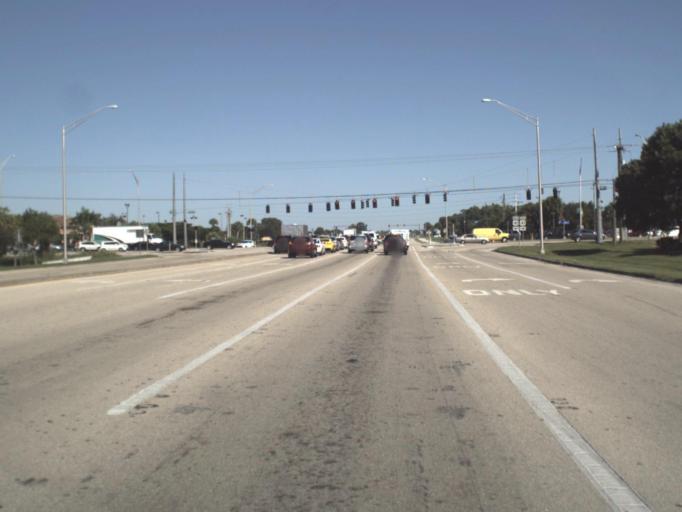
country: US
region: Florida
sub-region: Lee County
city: Villas
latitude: 26.5278
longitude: -81.8727
